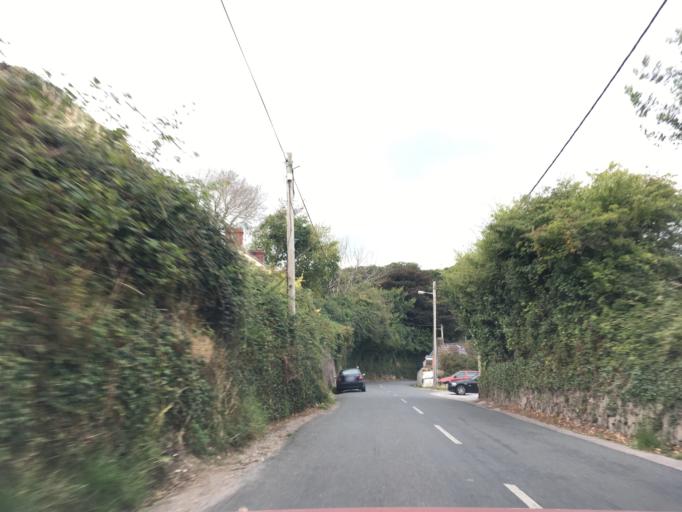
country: IE
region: Munster
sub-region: County Cork
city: Crosshaven
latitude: 51.8023
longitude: -8.2931
